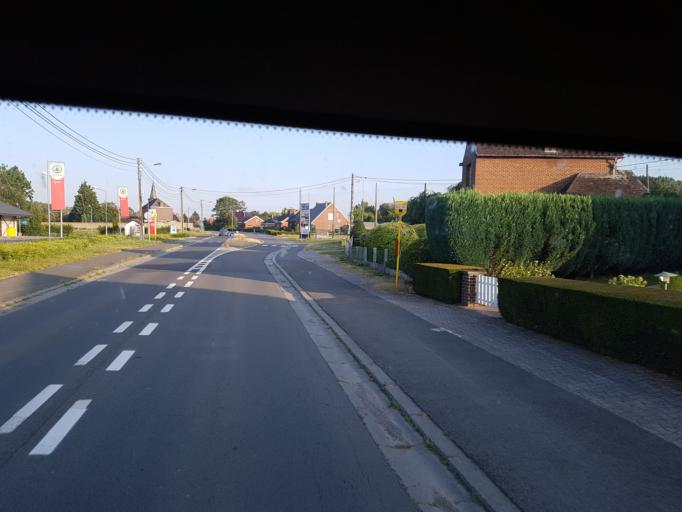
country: FR
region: Nord-Pas-de-Calais
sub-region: Departement du Nord
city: Hergnies
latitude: 50.5129
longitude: 3.5276
